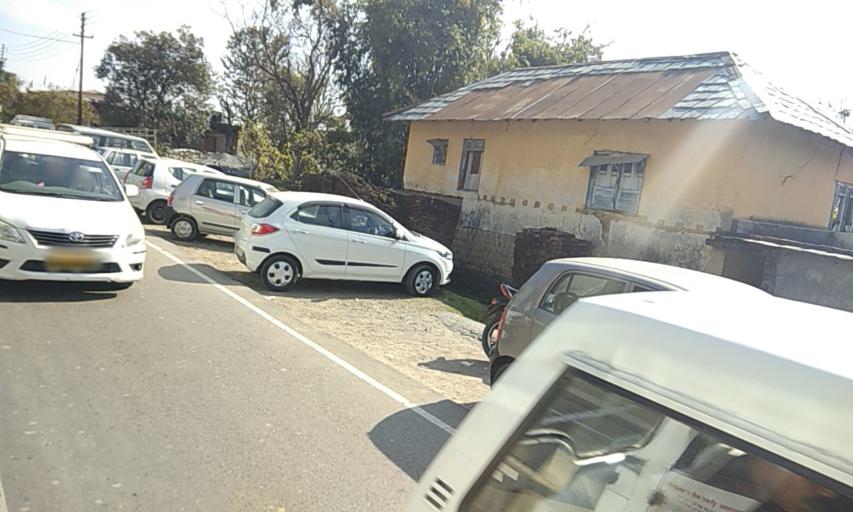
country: IN
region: Himachal Pradesh
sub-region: Kangra
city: Dharmsala
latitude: 32.1716
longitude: 76.3890
